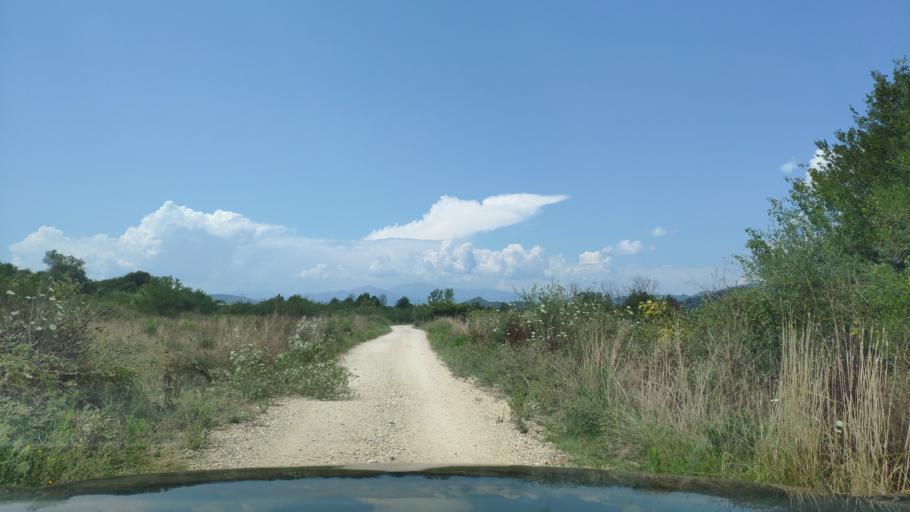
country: GR
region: West Greece
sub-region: Nomos Aitolias kai Akarnanias
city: Menidi
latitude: 39.0556
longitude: 21.0956
